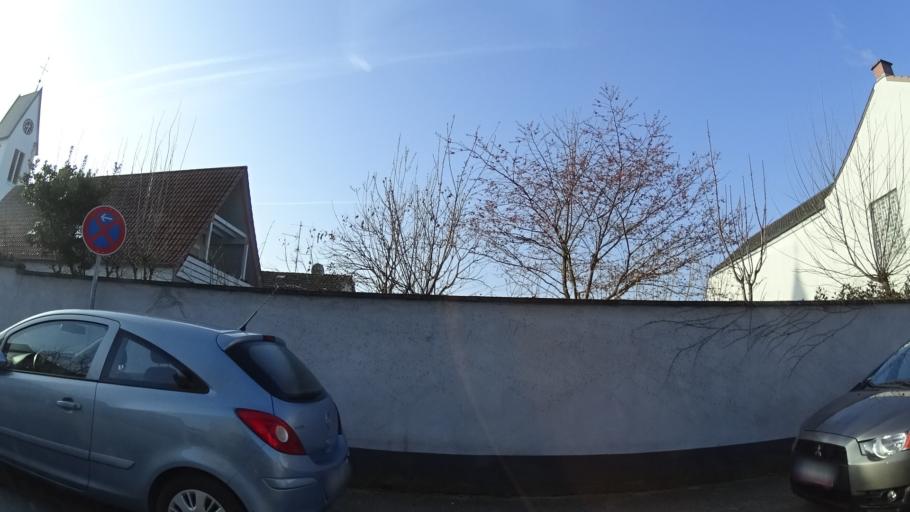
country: DE
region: Hesse
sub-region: Regierungsbezirk Darmstadt
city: Einhausen
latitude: 49.6753
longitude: 8.5479
